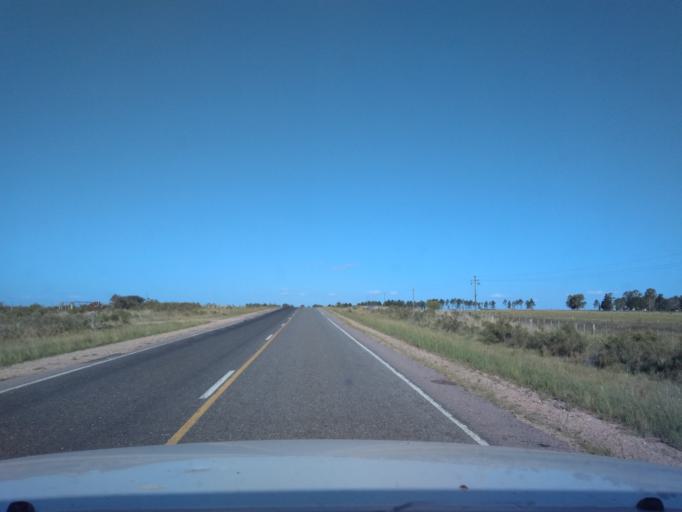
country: UY
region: Canelones
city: San Ramon
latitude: -34.0416
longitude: -55.9479
